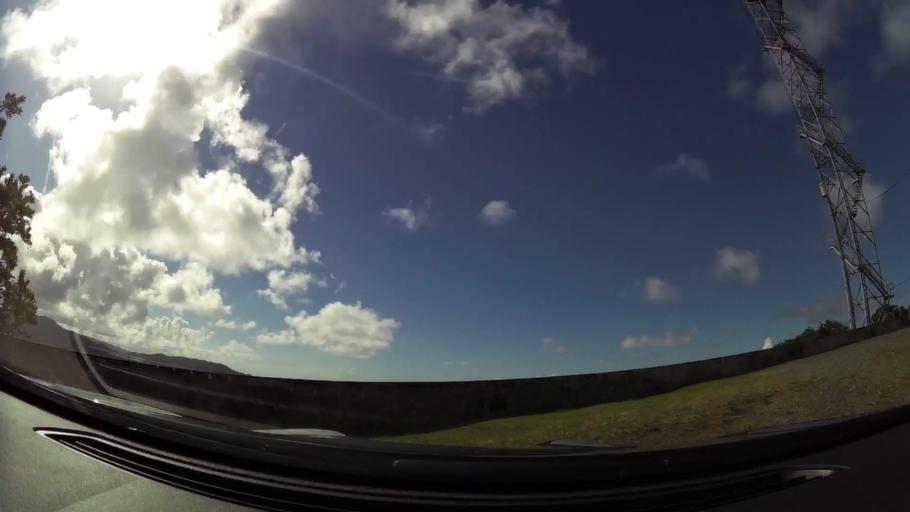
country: TT
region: Eastern Tobago
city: Roxborough
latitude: 11.3293
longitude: -60.5400
